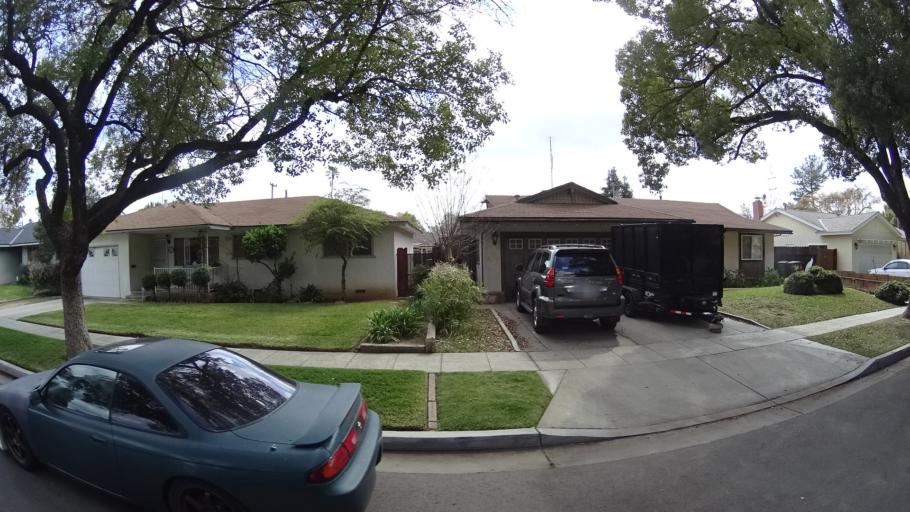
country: US
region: California
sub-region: Fresno County
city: Fresno
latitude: 36.8135
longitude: -119.7683
